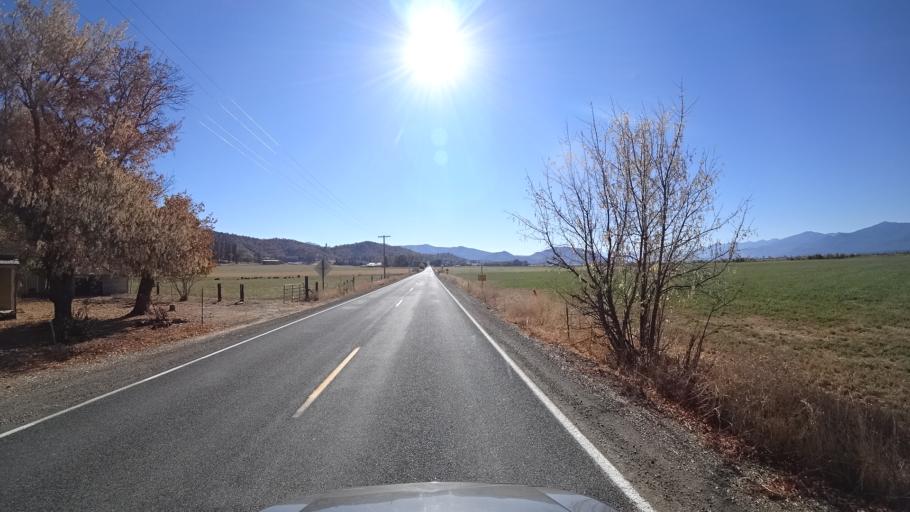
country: US
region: California
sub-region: Siskiyou County
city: Yreka
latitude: 41.5994
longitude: -122.8453
